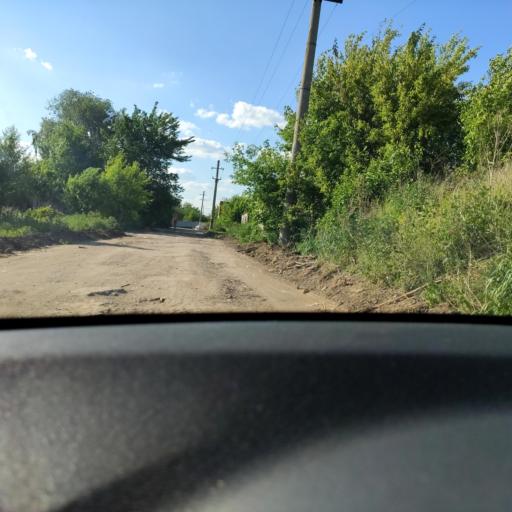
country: RU
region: Samara
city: Smyshlyayevka
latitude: 53.2440
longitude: 50.3572
